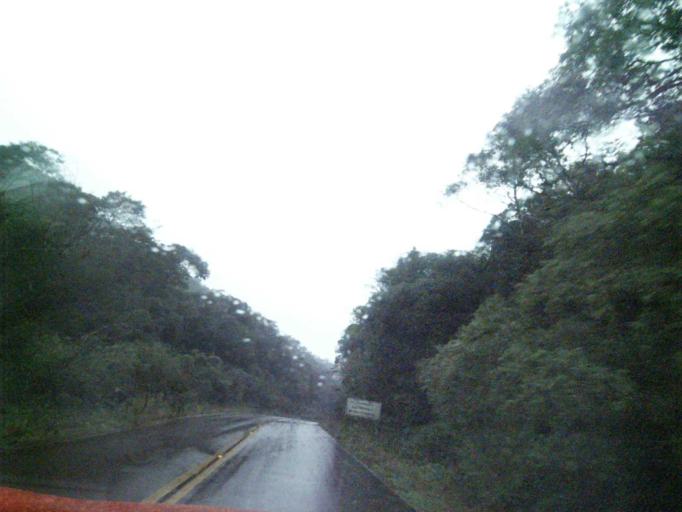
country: BR
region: Santa Catarina
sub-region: Anitapolis
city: Anitapolis
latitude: -27.7721
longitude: -49.0408
